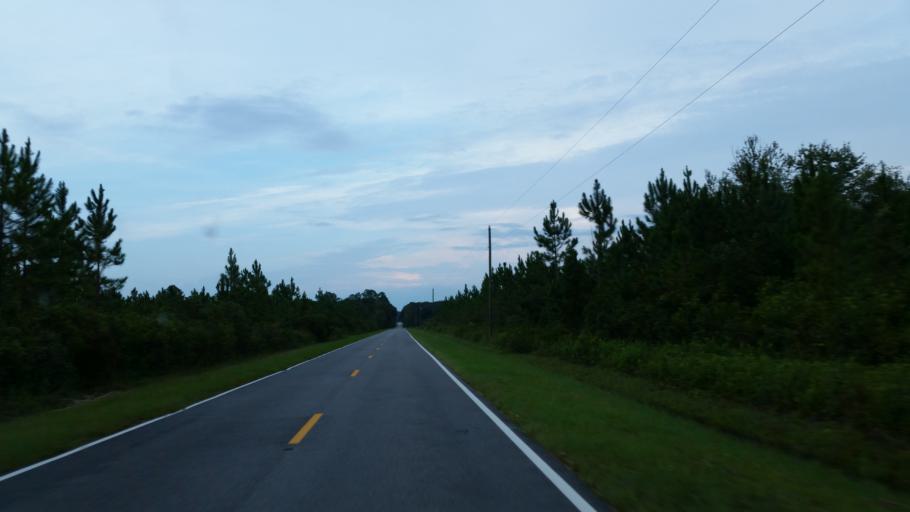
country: US
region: Georgia
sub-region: Lowndes County
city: Valdosta
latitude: 30.7458
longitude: -83.2457
